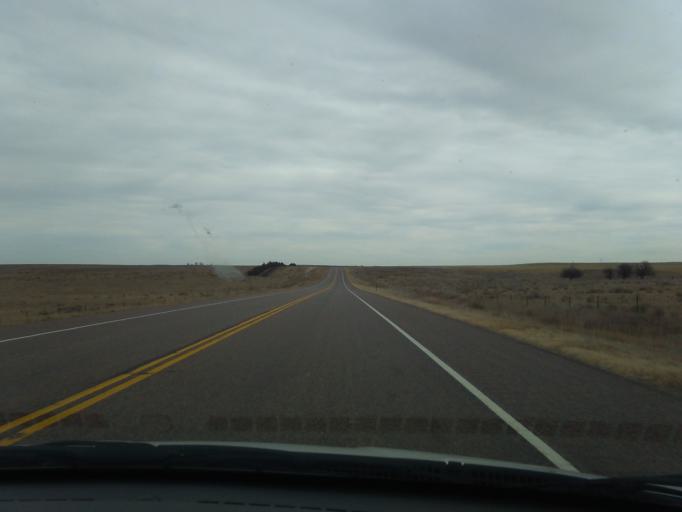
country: US
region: Colorado
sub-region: Yuma County
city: Wray
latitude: 40.0920
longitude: -102.3526
